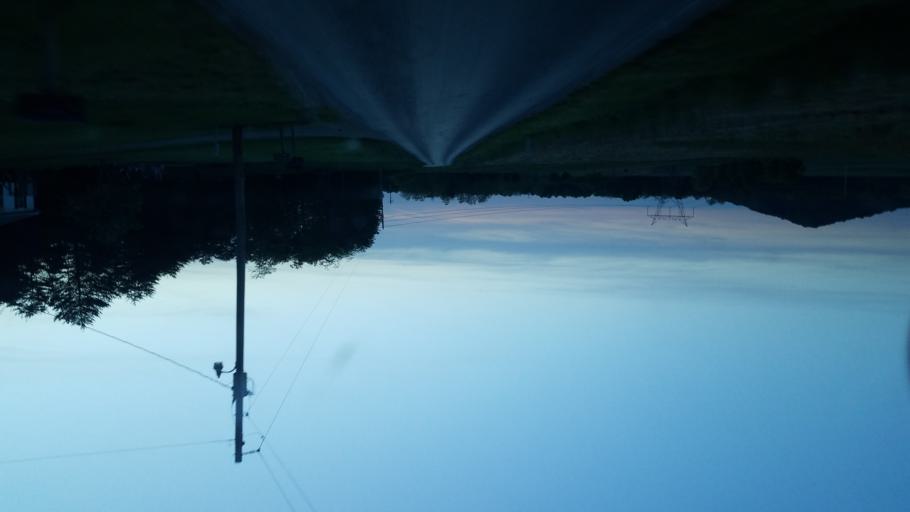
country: US
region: Ohio
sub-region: Highland County
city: Greenfield
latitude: 39.2049
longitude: -83.3572
